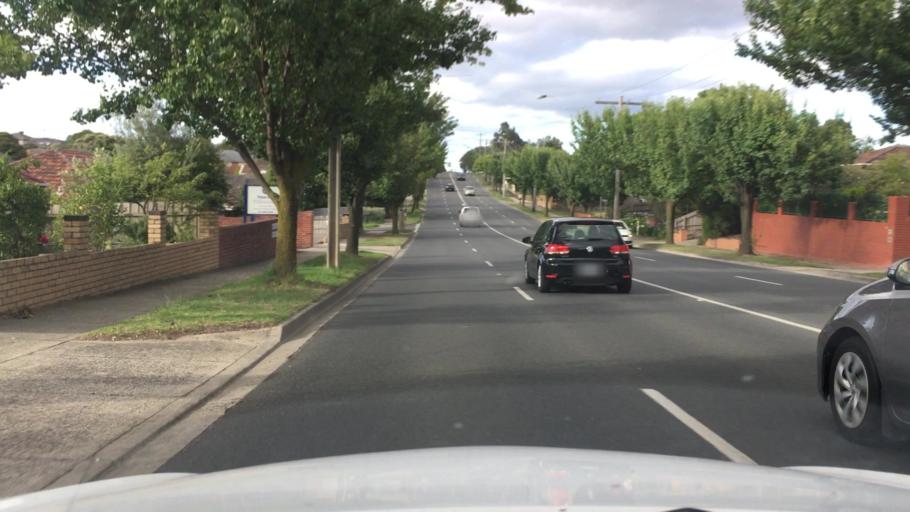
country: AU
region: Victoria
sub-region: Whitehorse
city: Burwood
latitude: -37.8558
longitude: 145.1317
